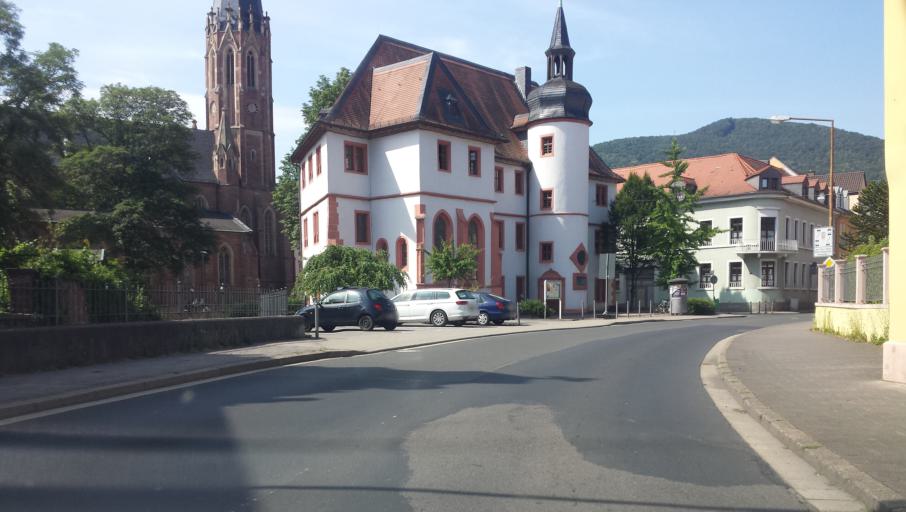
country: DE
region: Rheinland-Pfalz
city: Neustadt
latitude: 49.3540
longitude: 8.1348
